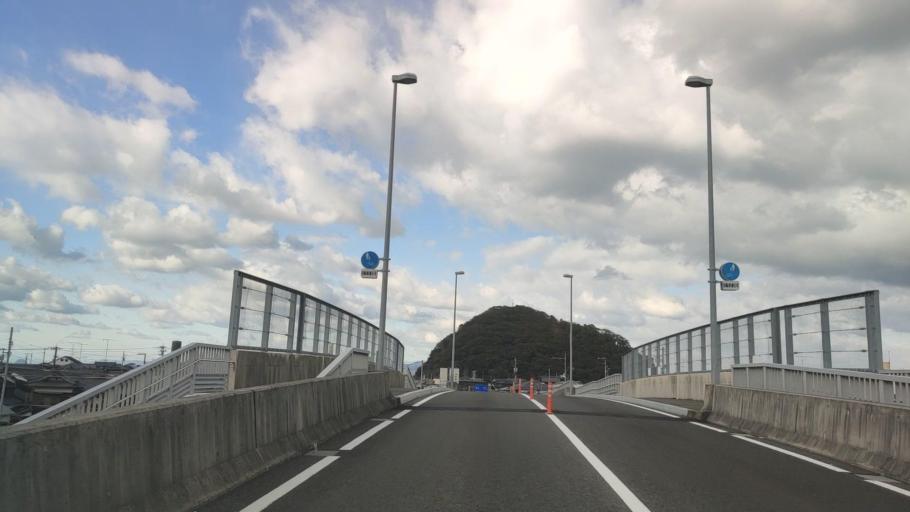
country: JP
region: Ehime
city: Hojo
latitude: 33.9714
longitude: 132.7752
